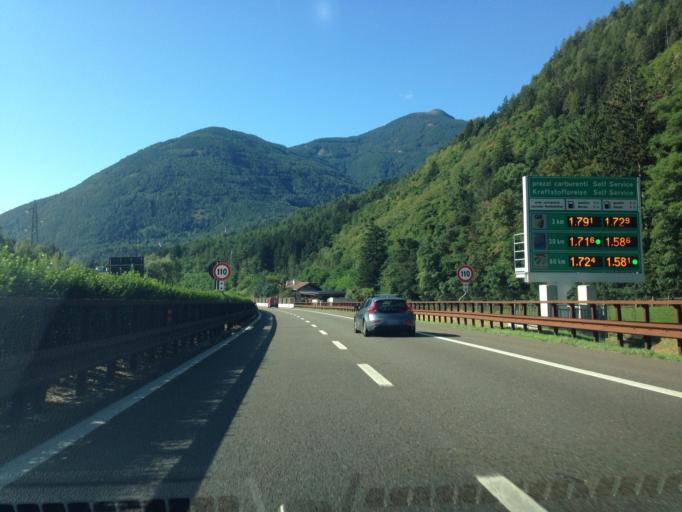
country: IT
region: Trentino-Alto Adige
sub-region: Bolzano
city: Varna
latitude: 46.7572
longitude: 11.6346
